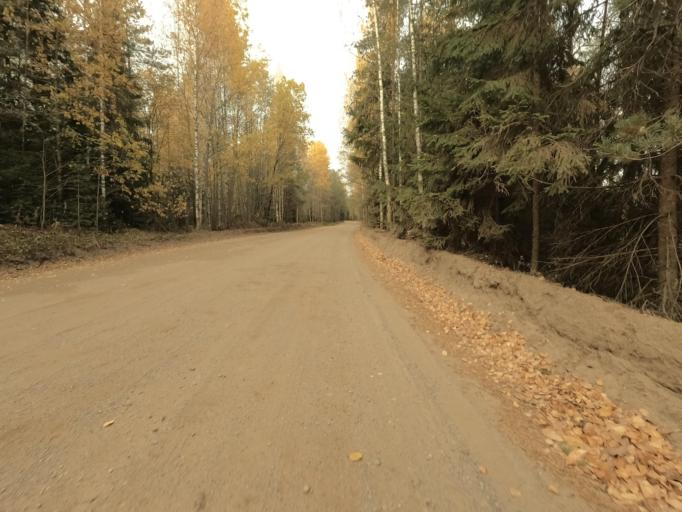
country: RU
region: Leningrad
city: Priladozhskiy
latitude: 59.6851
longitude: 31.3621
